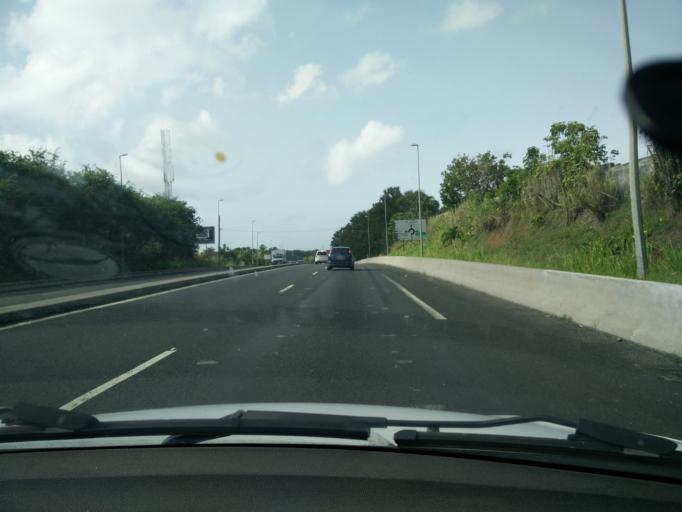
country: GP
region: Guadeloupe
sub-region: Guadeloupe
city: Baie-Mahault
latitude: 16.2576
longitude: -61.5709
